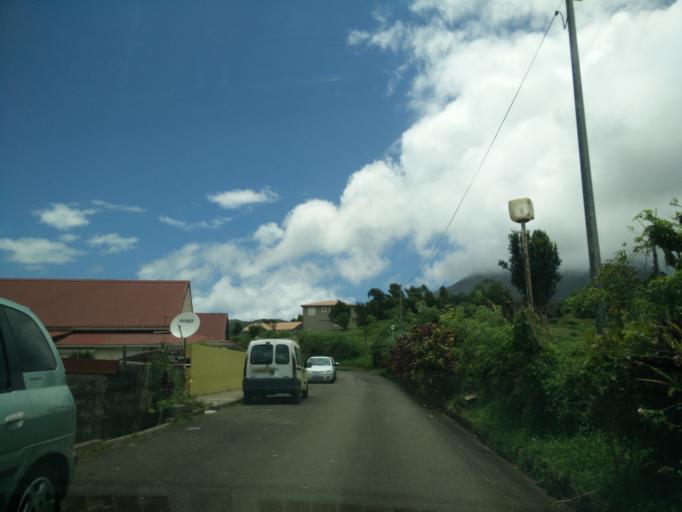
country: MQ
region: Martinique
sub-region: Martinique
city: Le Morne-Rouge
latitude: 14.7845
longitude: -61.1389
